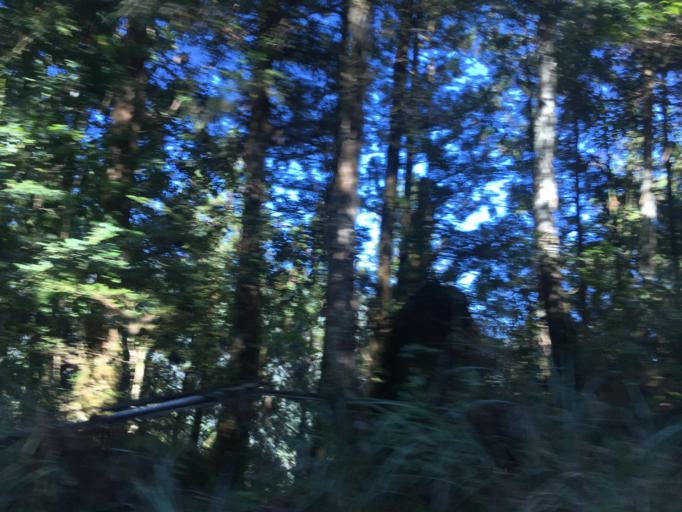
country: TW
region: Taiwan
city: Daxi
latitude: 24.6020
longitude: 121.4525
